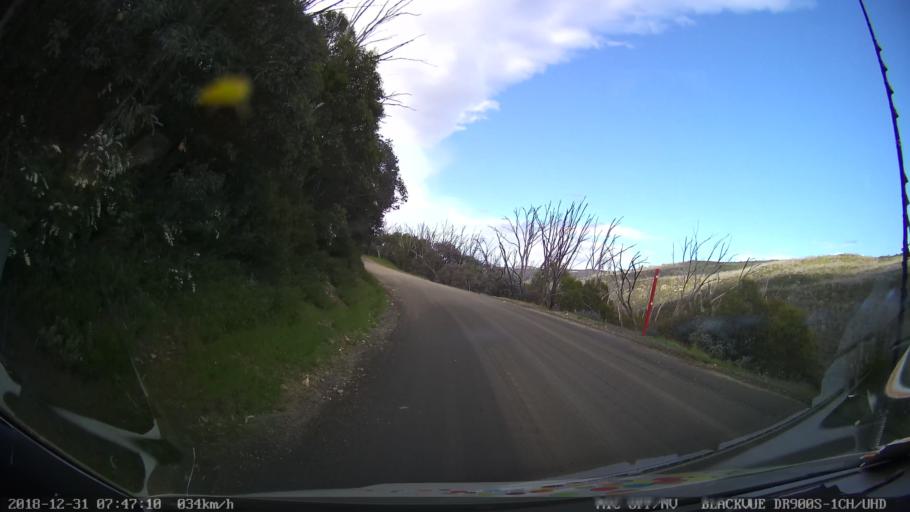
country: AU
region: New South Wales
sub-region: Snowy River
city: Jindabyne
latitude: -36.3626
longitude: 148.3970
